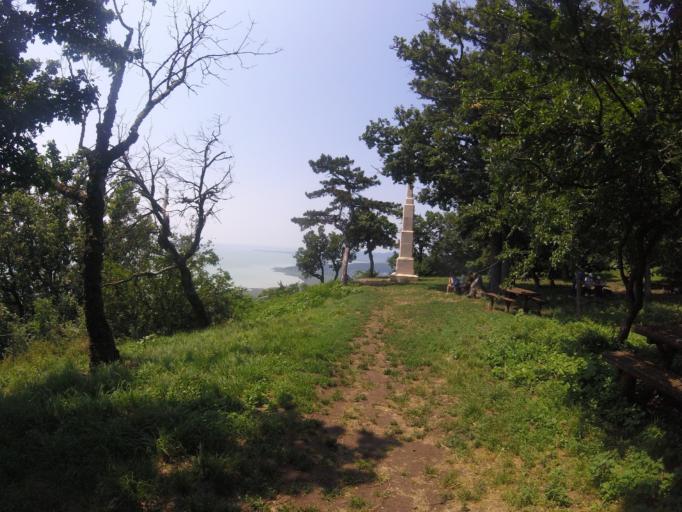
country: HU
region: Veszprem
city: Badacsonytomaj
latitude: 46.7968
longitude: 17.4908
